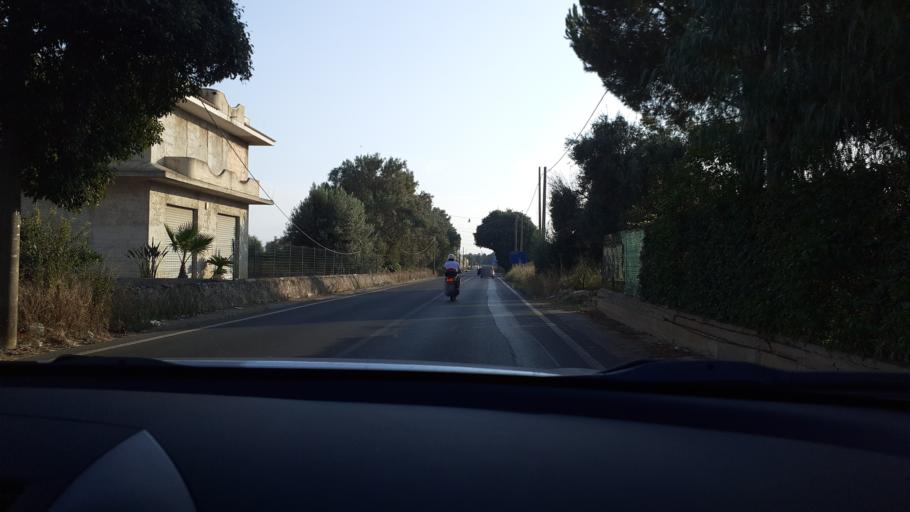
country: IT
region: Sicily
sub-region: Provincia di Siracusa
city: Cassibile
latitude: 36.9746
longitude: 15.1951
